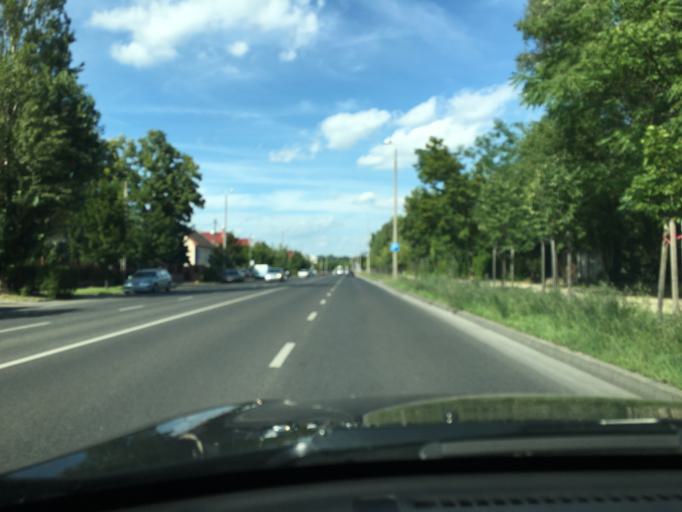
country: HU
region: Budapest
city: Budapest IV. keruelet
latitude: 47.5837
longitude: 19.0923
